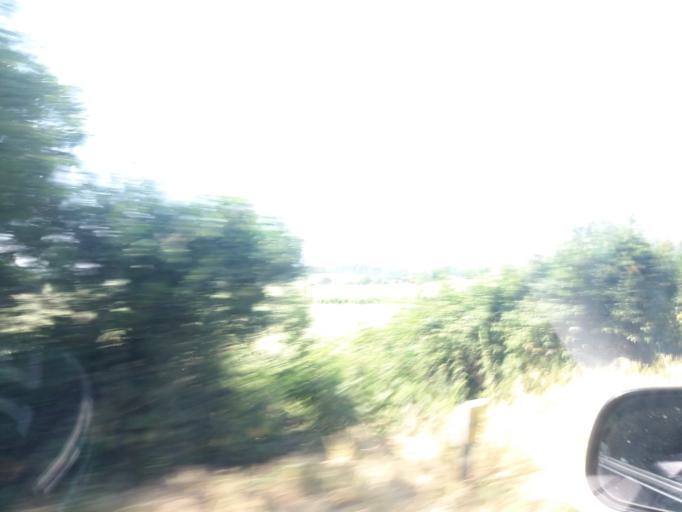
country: IE
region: Leinster
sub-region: An Mhi
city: Stamullin
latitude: 53.5664
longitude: -6.3164
